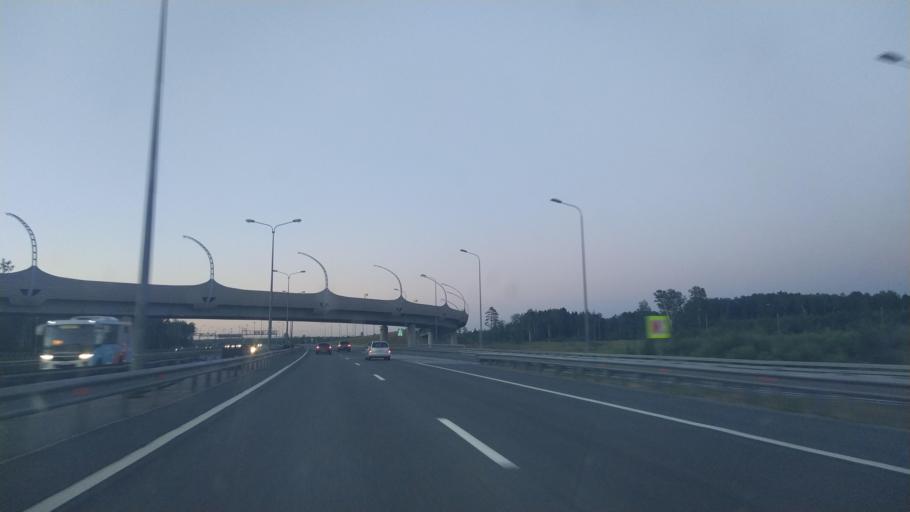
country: RU
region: St.-Petersburg
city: Ol'gino
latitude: 60.0597
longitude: 30.1498
